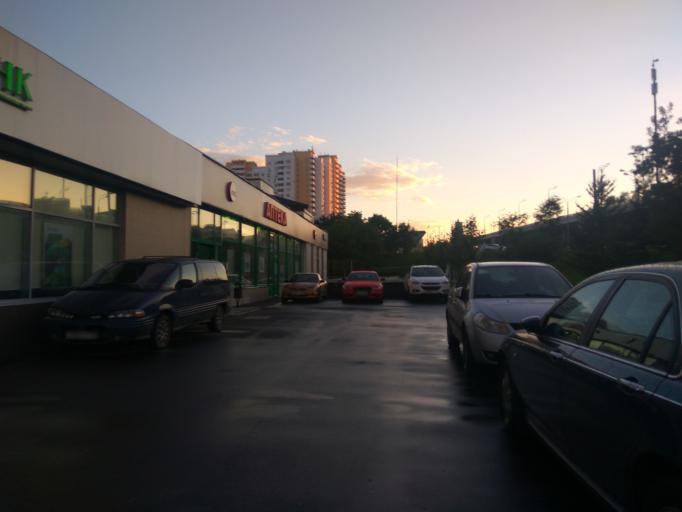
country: RU
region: Moskovskaya
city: Bol'shaya Setun'
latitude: 55.7173
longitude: 37.4119
